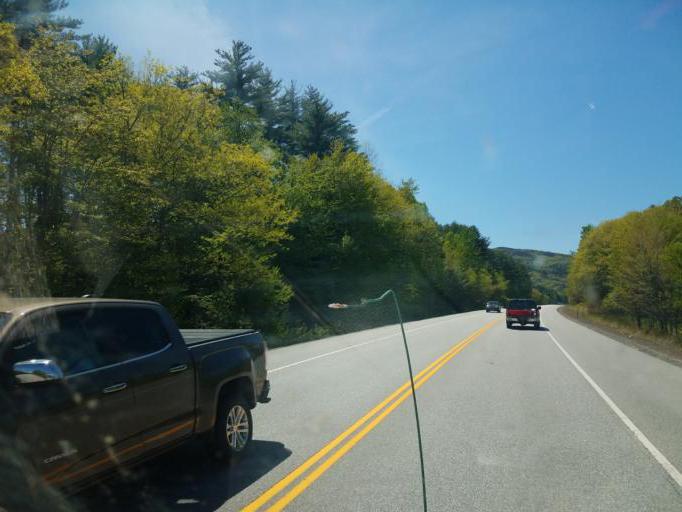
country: US
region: New Hampshire
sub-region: Grafton County
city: Rumney
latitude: 43.7948
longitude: -71.8313
